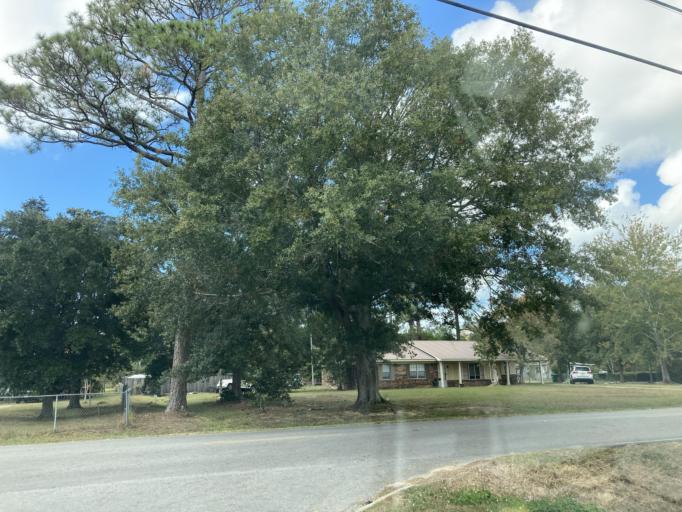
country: US
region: Mississippi
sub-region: Jackson County
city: Gulf Hills
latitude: 30.4470
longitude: -88.8302
